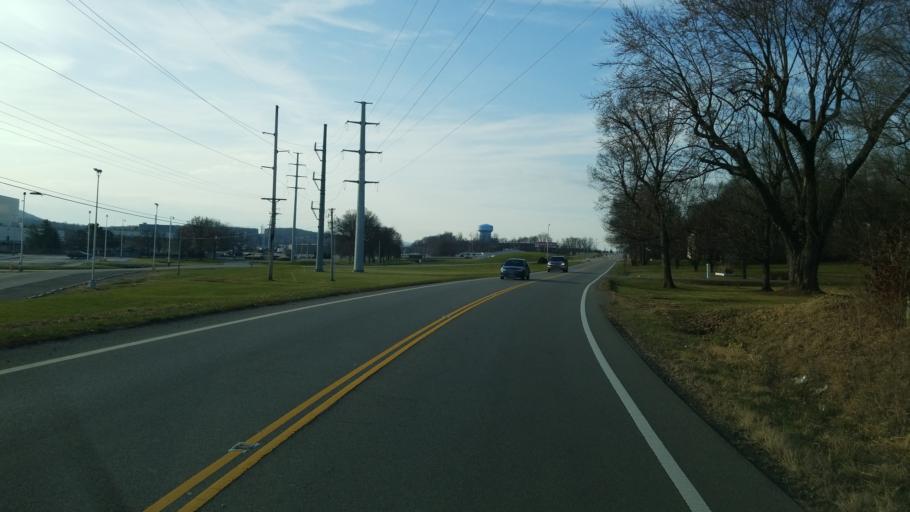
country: US
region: Ohio
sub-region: Ross County
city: Chillicothe
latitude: 39.4012
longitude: -82.9616
